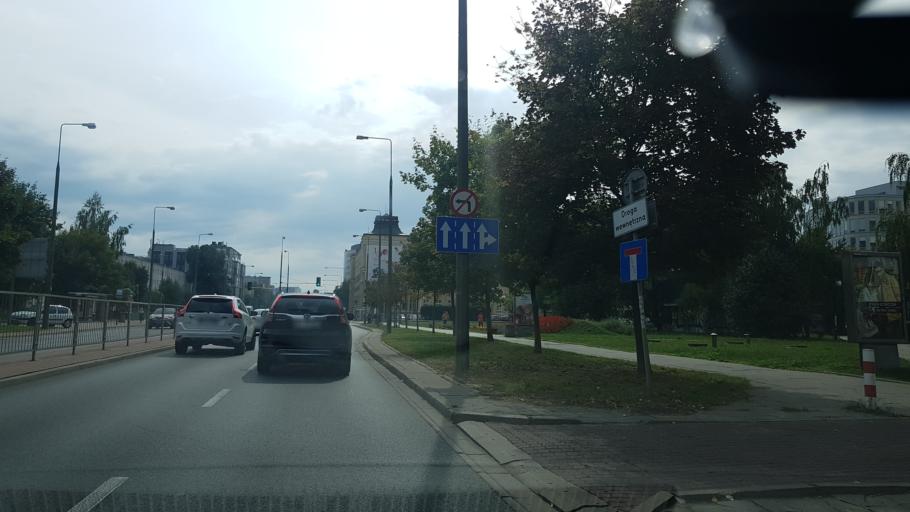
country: PL
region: Masovian Voivodeship
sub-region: Warszawa
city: Mokotow
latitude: 52.1942
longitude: 21.0144
